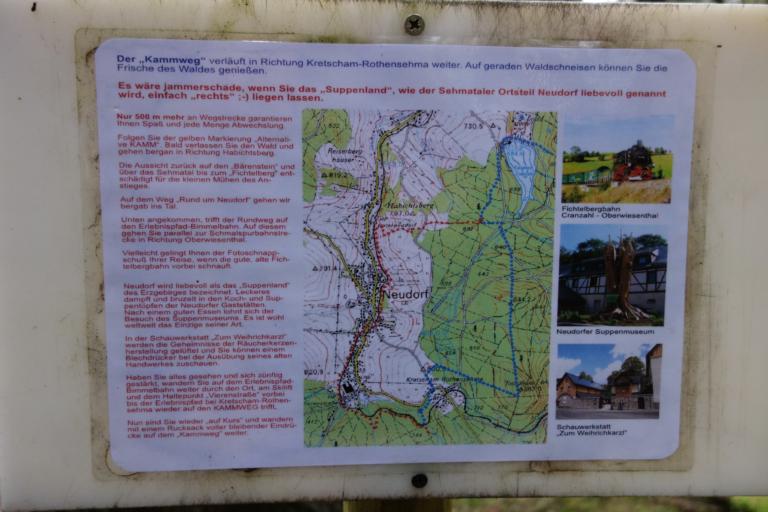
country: CZ
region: Ustecky
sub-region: Okres Chomutov
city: Vejprty
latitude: 50.4929
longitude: 12.9974
